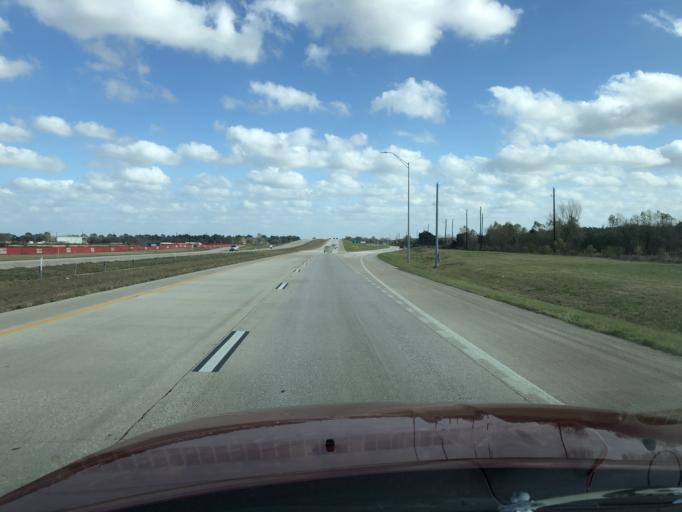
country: US
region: Texas
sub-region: Harris County
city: Cypress
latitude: 30.0536
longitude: -95.7042
